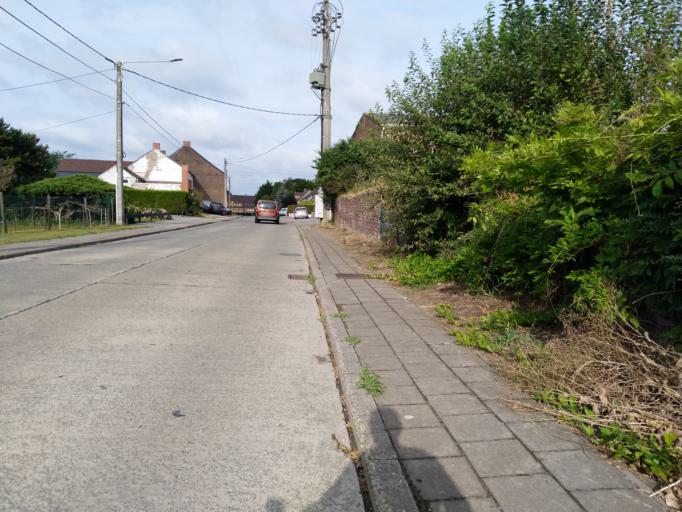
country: BE
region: Wallonia
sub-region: Province du Hainaut
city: Jurbise
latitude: 50.5316
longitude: 3.9080
